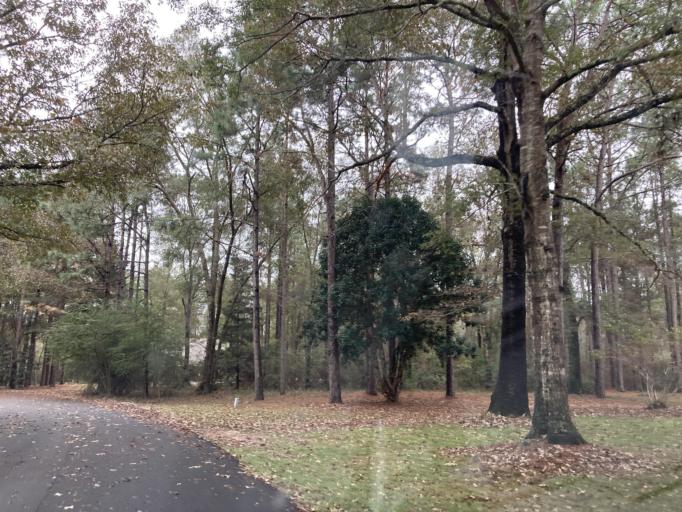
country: US
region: Mississippi
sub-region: Lamar County
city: Purvis
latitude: 31.1542
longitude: -89.4221
